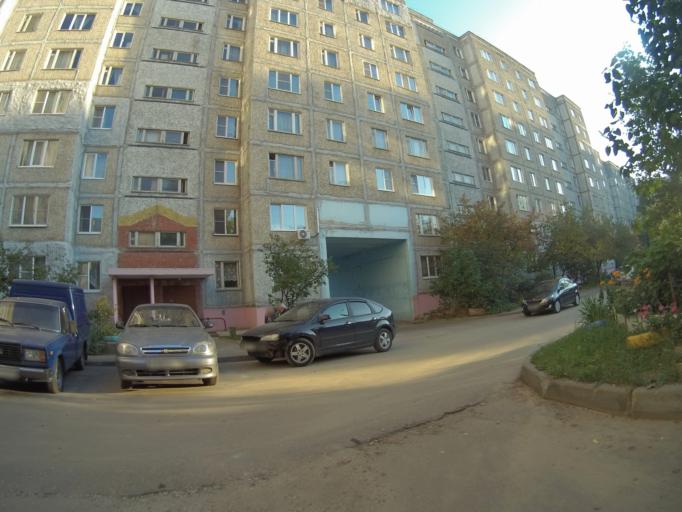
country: RU
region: Vladimir
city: Vladimir
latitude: 56.1076
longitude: 40.3549
